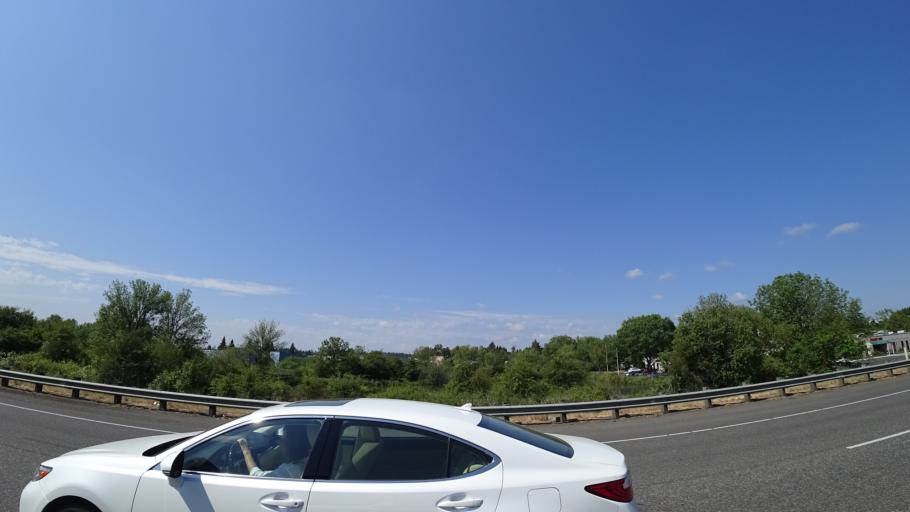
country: US
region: Oregon
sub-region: Washington County
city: Tigard
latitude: 45.4319
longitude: -122.7587
